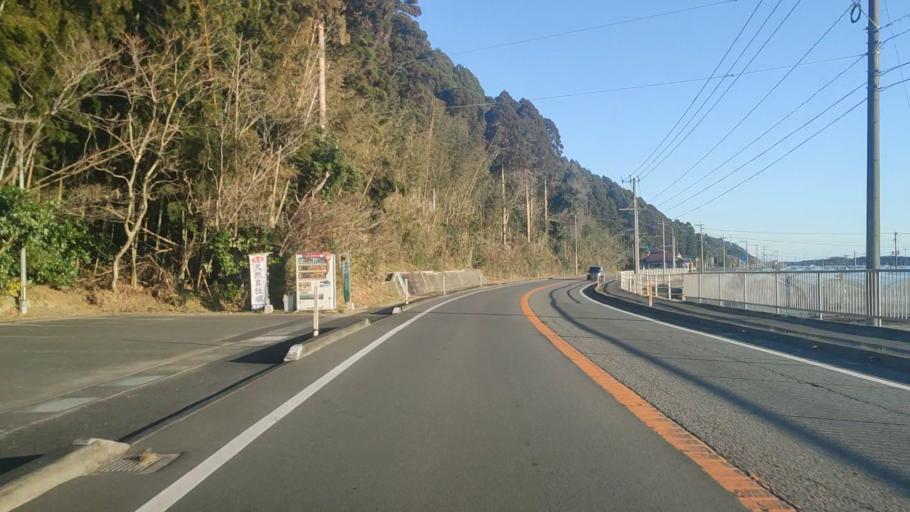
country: JP
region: Miyazaki
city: Takanabe
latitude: 32.0873
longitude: 131.5123
